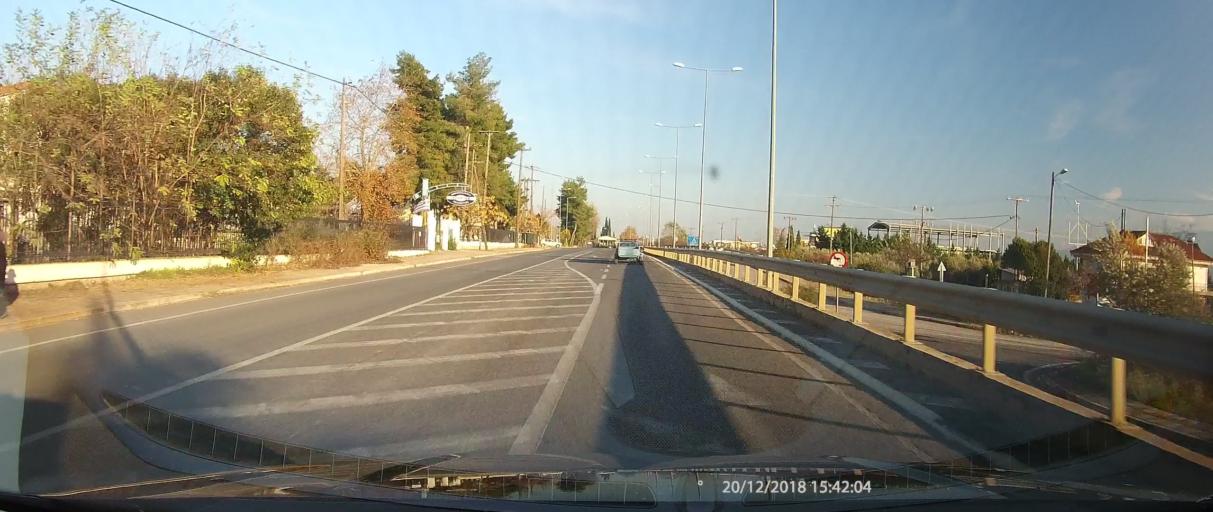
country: GR
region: Central Greece
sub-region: Nomos Fthiotidos
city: Stavros
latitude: 38.8893
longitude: 22.3941
